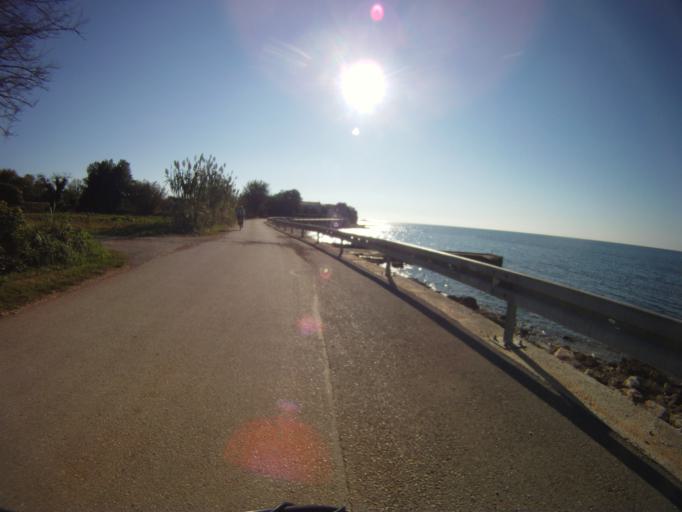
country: HR
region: Istarska
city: Umag
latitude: 45.3994
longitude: 13.5347
